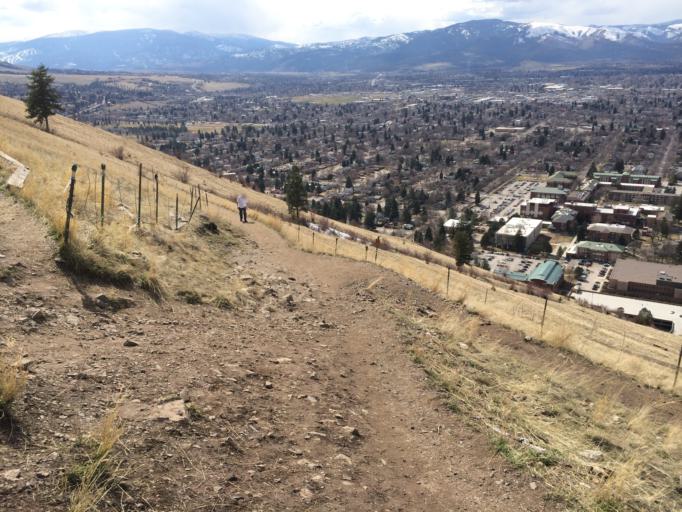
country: US
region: Montana
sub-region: Missoula County
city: Missoula
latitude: 46.8595
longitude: -113.9757
